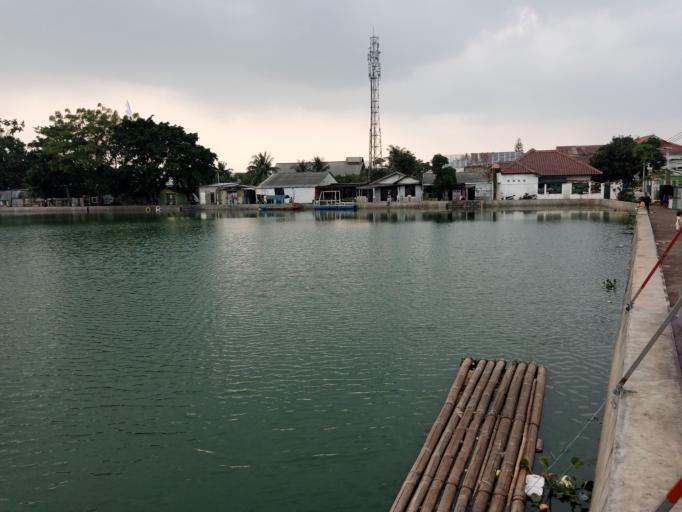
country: ID
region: West Java
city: Depok
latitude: -6.3913
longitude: 106.8175
